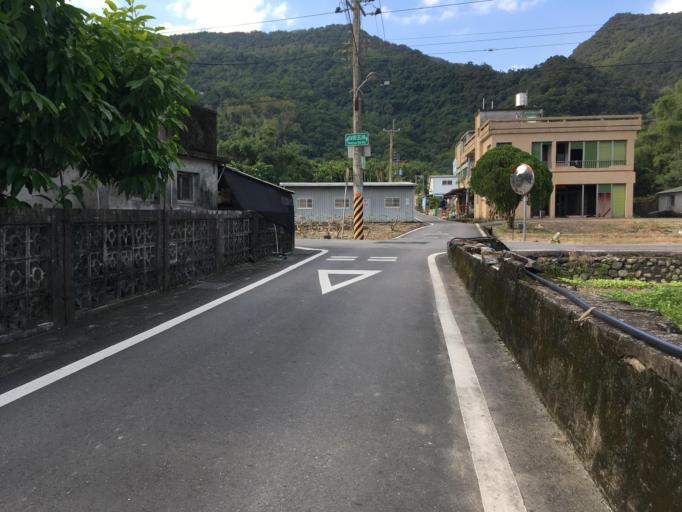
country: TW
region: Taiwan
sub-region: Yilan
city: Yilan
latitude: 24.8383
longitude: 121.7833
